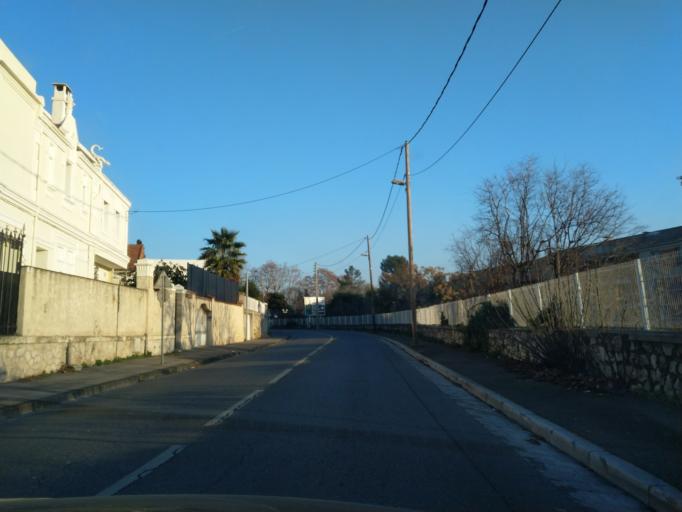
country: FR
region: Provence-Alpes-Cote d'Azur
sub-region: Departement des Bouches-du-Rhone
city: Marseille 12
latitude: 43.3041
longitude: 5.4350
